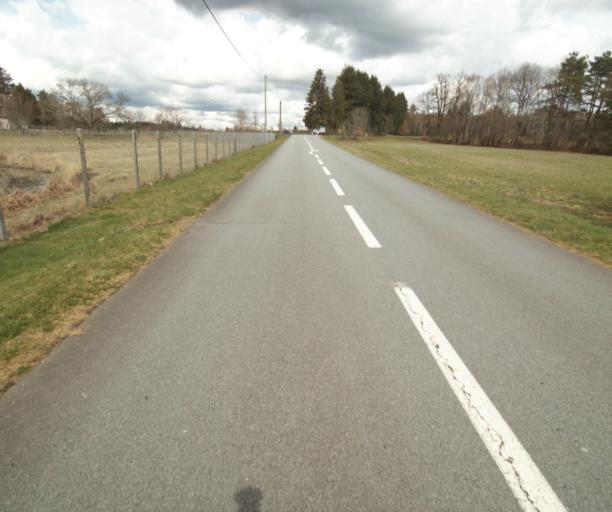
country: FR
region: Limousin
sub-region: Departement de la Correze
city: Correze
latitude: 45.3442
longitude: 1.9466
